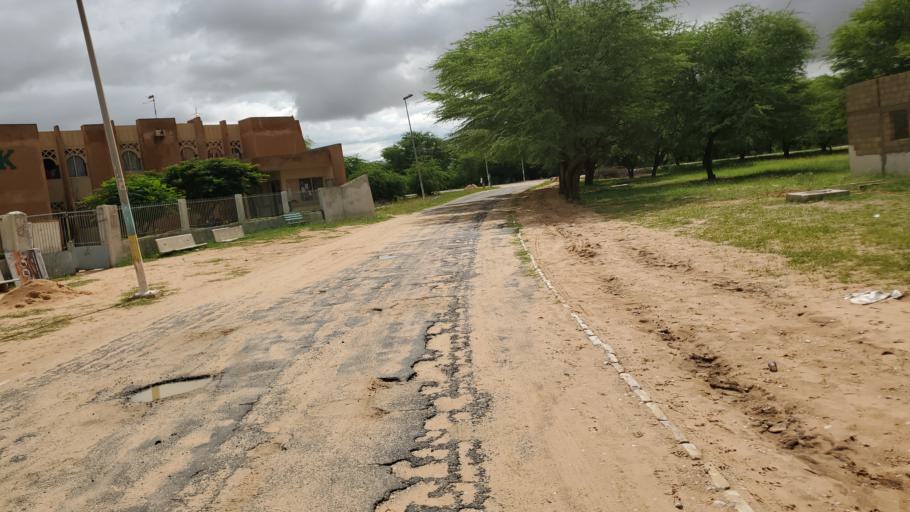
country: SN
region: Saint-Louis
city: Saint-Louis
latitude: 16.0618
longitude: -16.4274
